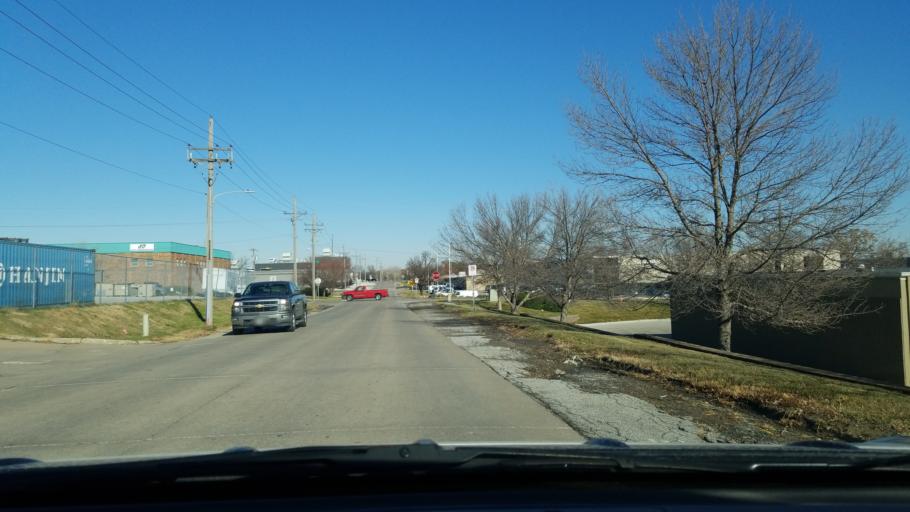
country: US
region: Nebraska
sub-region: Douglas County
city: Ralston
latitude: 41.2135
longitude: -96.0719
